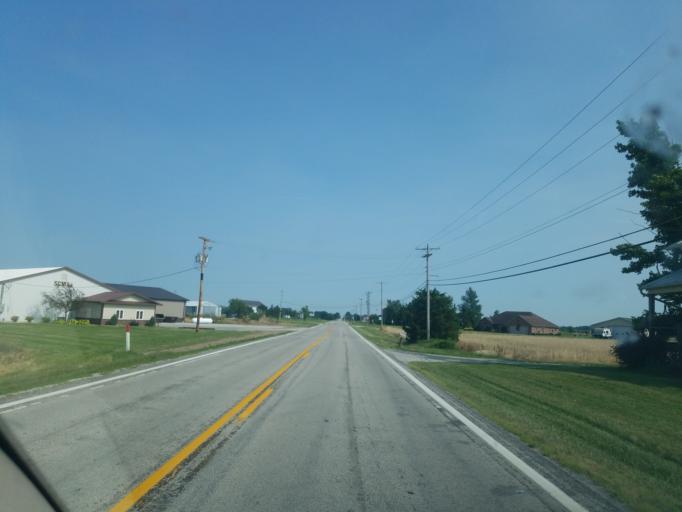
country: US
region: Ohio
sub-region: Wyandot County
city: Carey
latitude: 41.0446
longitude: -83.3122
